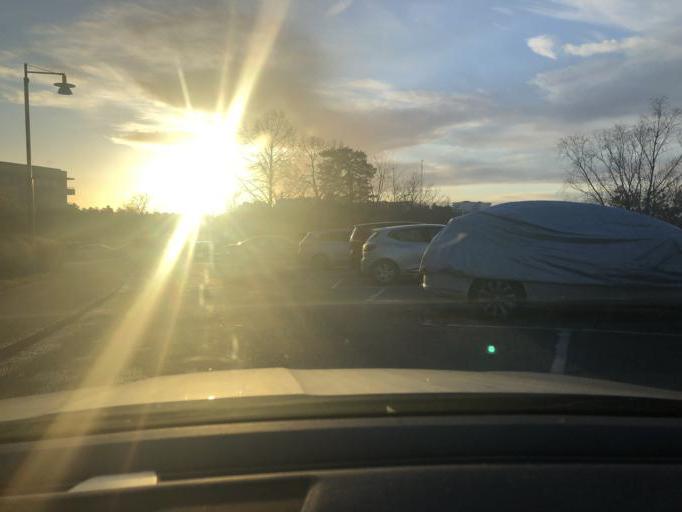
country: SE
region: Stockholm
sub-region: Huddinge Kommun
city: Segeltorp
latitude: 59.2836
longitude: 17.9168
